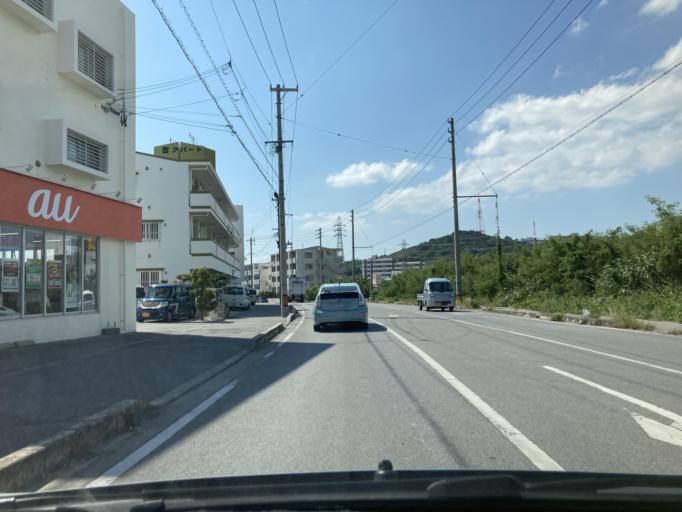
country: JP
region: Okinawa
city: Tomigusuku
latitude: 26.1908
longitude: 127.7120
